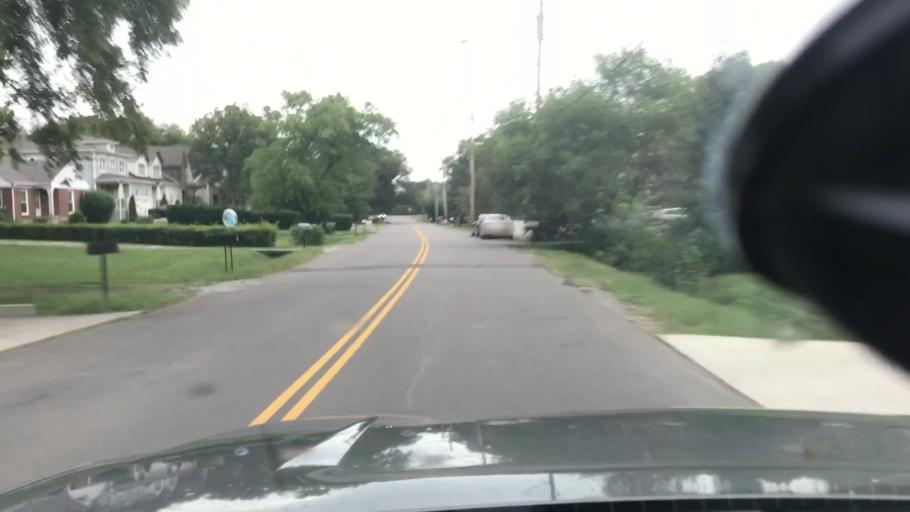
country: US
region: Tennessee
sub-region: Davidson County
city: Oak Hill
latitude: 36.1152
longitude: -86.7954
